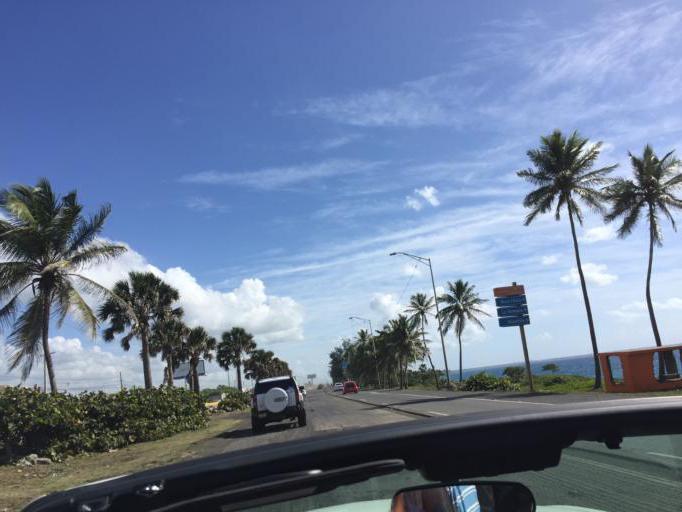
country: DO
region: Santo Domingo
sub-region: Santo Domingo
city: Santo Domingo Este
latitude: 18.4636
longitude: -69.7523
